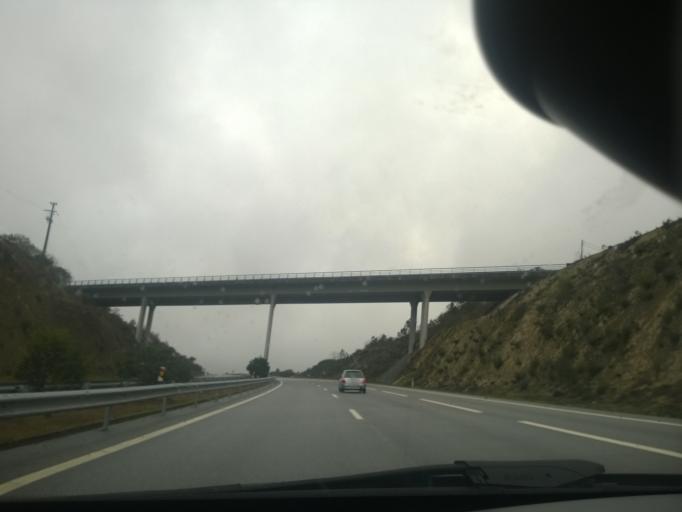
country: PT
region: Braga
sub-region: Celorico de Basto
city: Celorico de Basto
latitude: 41.4480
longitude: -8.0698
